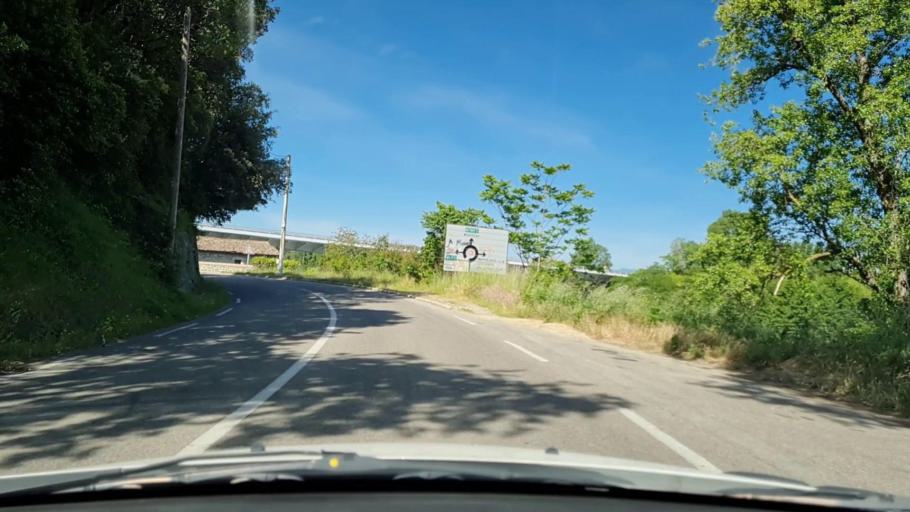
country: FR
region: Languedoc-Roussillon
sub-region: Departement du Gard
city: Vezenobres
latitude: 44.0167
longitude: 4.1565
